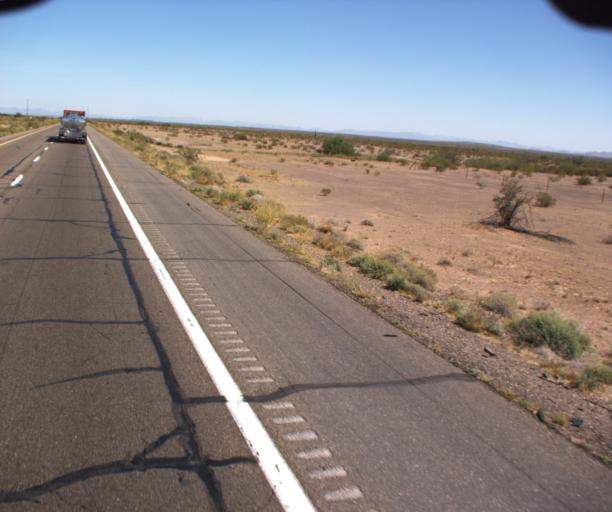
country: US
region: Arizona
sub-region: Maricopa County
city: Gila Bend
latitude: 32.8976
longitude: -113.0211
